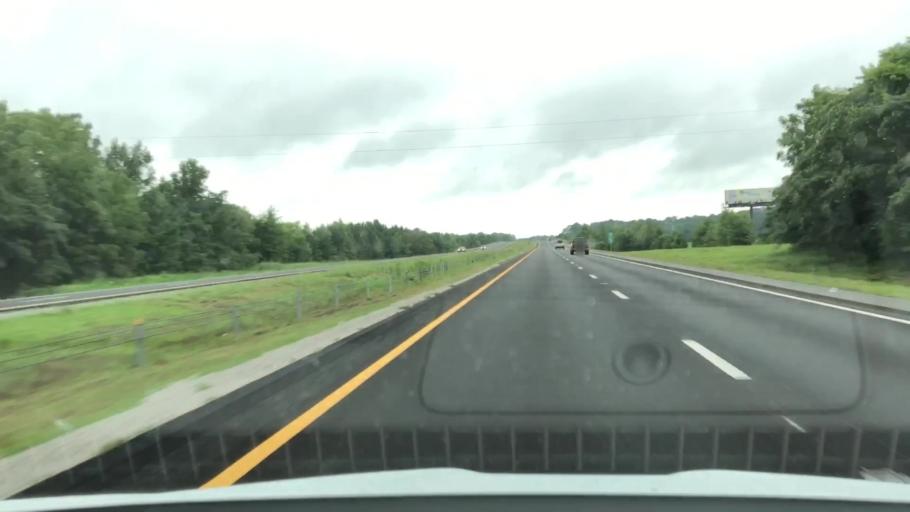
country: US
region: North Carolina
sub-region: Wayne County
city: Goldsboro
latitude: 35.4631
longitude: -77.9858
